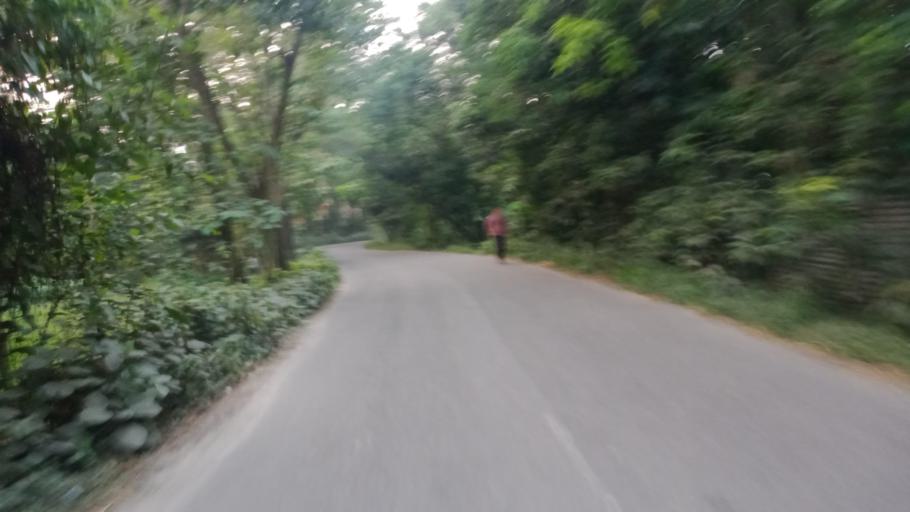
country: BD
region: Chittagong
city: Hajiganj
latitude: 23.3697
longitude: 90.9835
